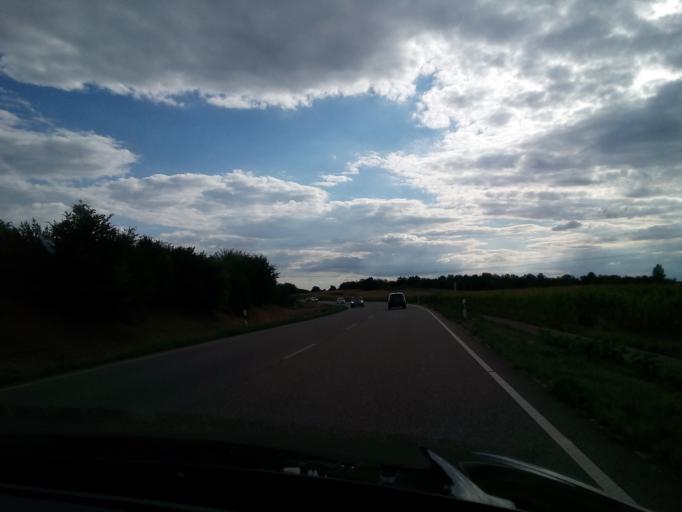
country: DE
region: Baden-Wuerttemberg
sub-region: Freiburg Region
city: Renchen
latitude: 48.5700
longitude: 7.9890
